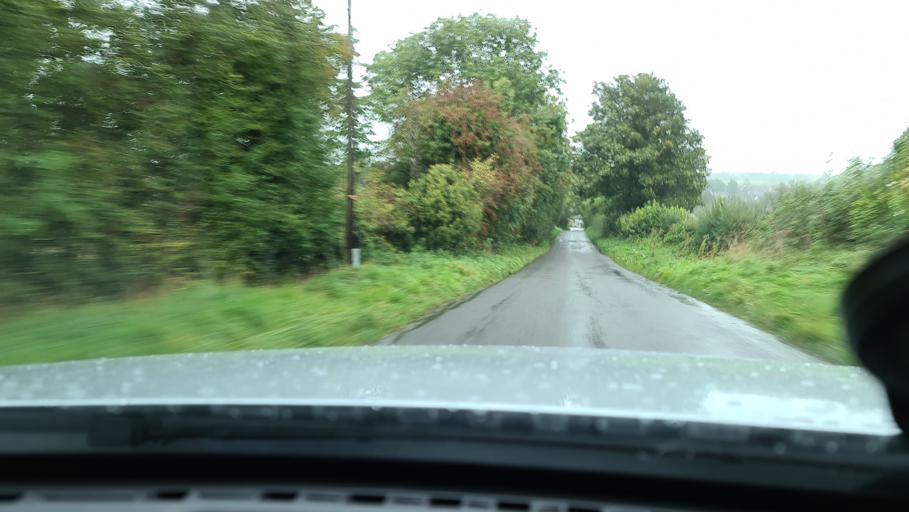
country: GB
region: England
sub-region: Oxfordshire
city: Deddington
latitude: 51.9242
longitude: -1.3678
